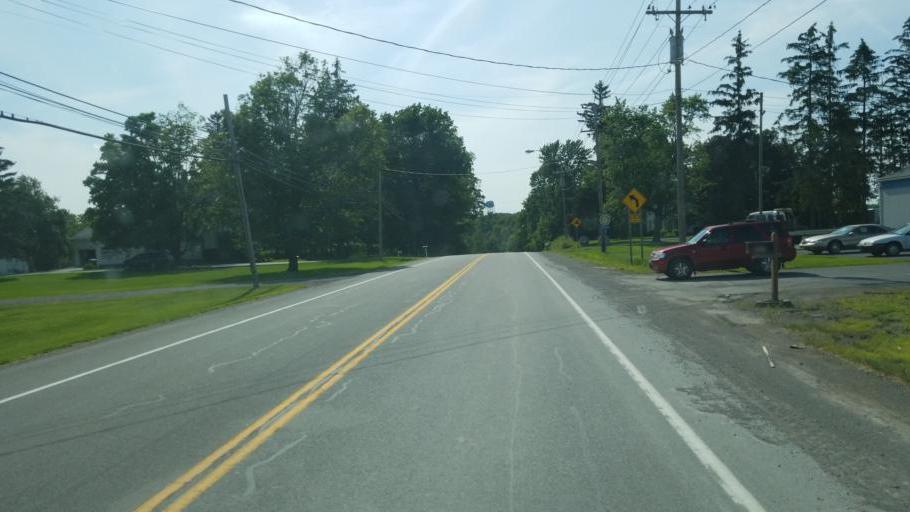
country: US
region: New York
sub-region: Livingston County
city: Lima
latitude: 42.9090
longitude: -77.5980
